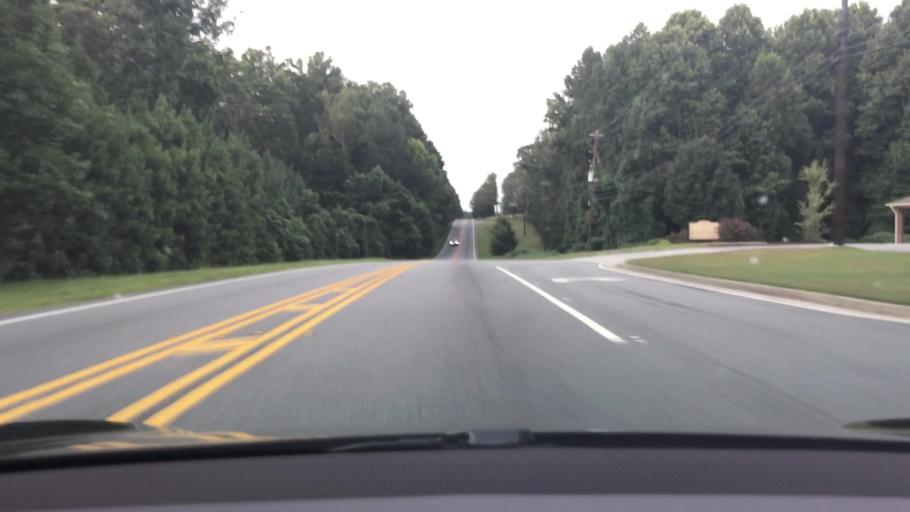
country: US
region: Georgia
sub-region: Gwinnett County
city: Duluth
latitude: 34.0137
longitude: -84.1263
